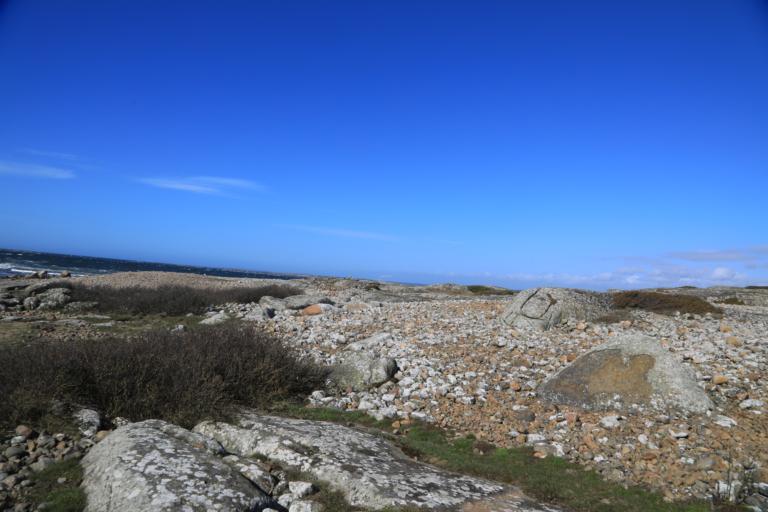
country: SE
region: Halland
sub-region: Varbergs Kommun
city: Varberg
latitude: 57.1158
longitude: 12.1907
